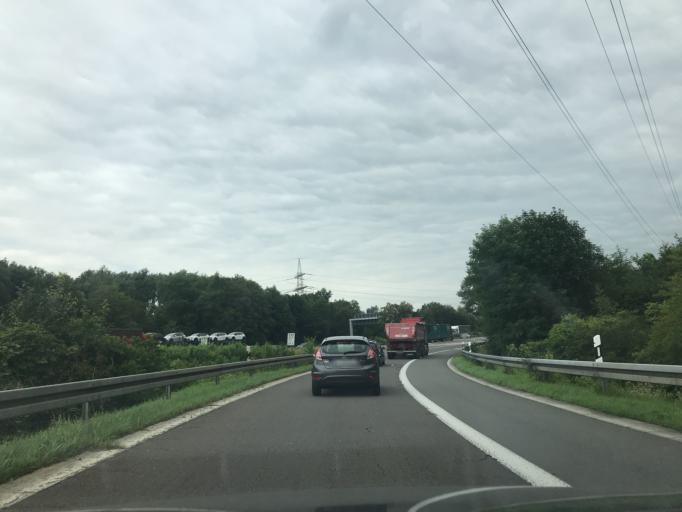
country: DE
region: North Rhine-Westphalia
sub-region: Regierungsbezirk Dusseldorf
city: Erkrath
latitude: 51.1893
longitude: 6.8727
